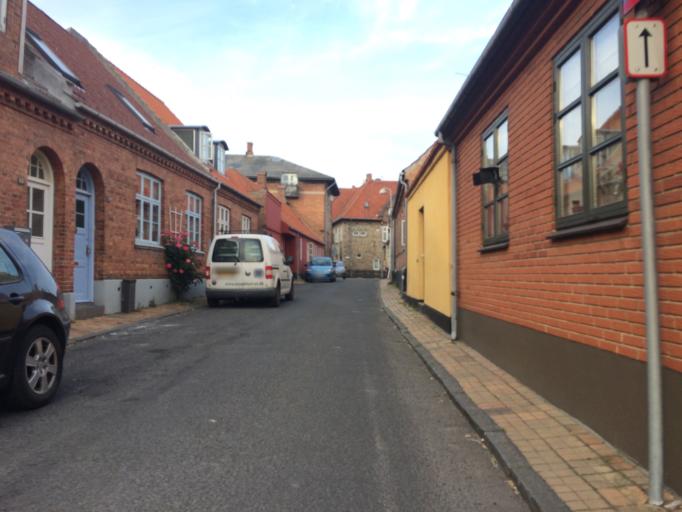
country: DK
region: Capital Region
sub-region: Bornholm Kommune
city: Ronne
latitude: 55.1002
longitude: 14.6998
